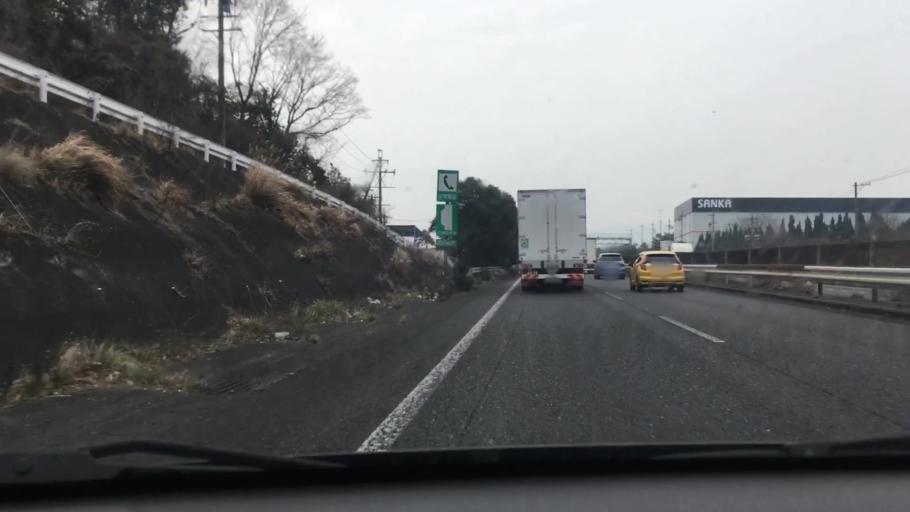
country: JP
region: Mie
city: Ueno-ebisumachi
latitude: 34.7962
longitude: 136.1733
